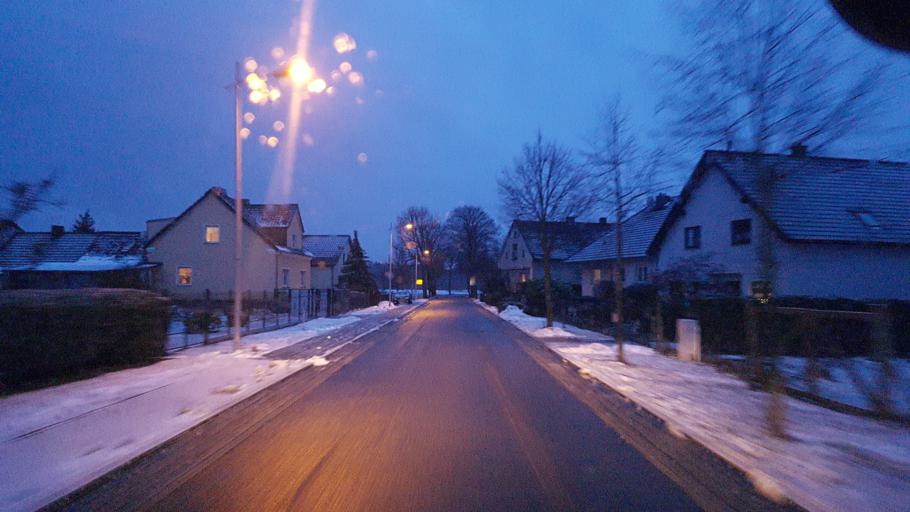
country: DE
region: Brandenburg
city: Guhrow
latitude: 51.7971
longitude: 14.2201
